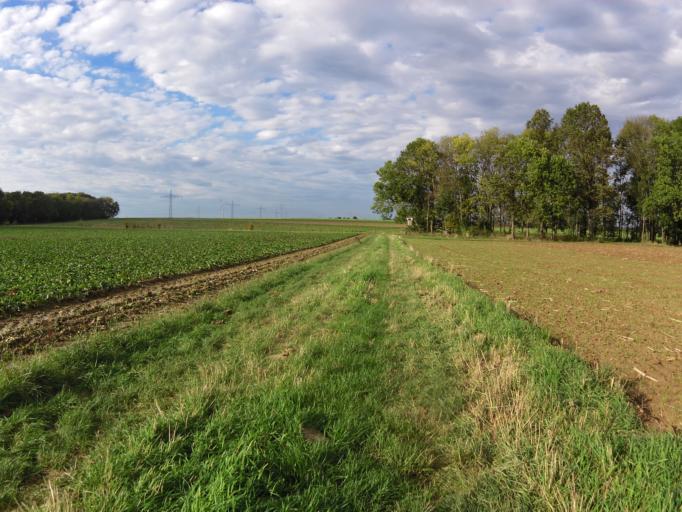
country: DE
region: Bavaria
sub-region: Regierungsbezirk Unterfranken
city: Biebelried
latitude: 49.7311
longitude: 10.0706
